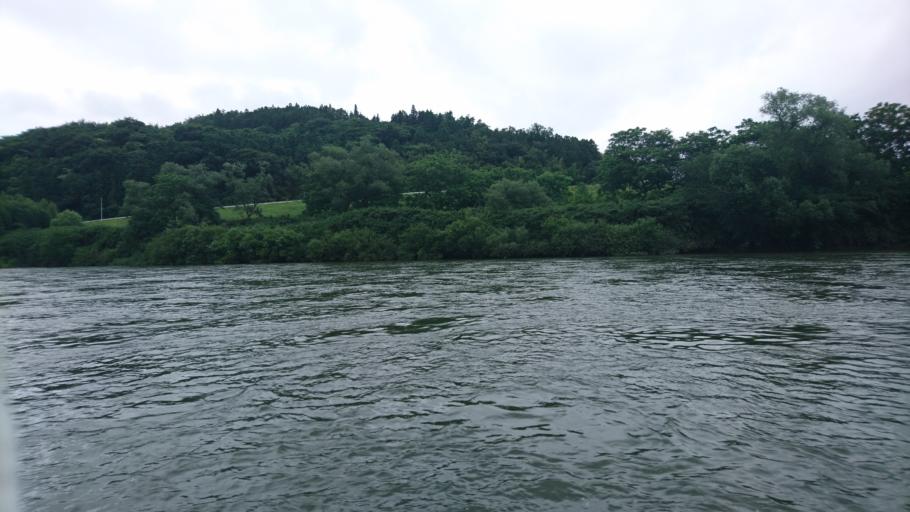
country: JP
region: Iwate
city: Ichinoseki
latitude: 38.9040
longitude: 141.2496
